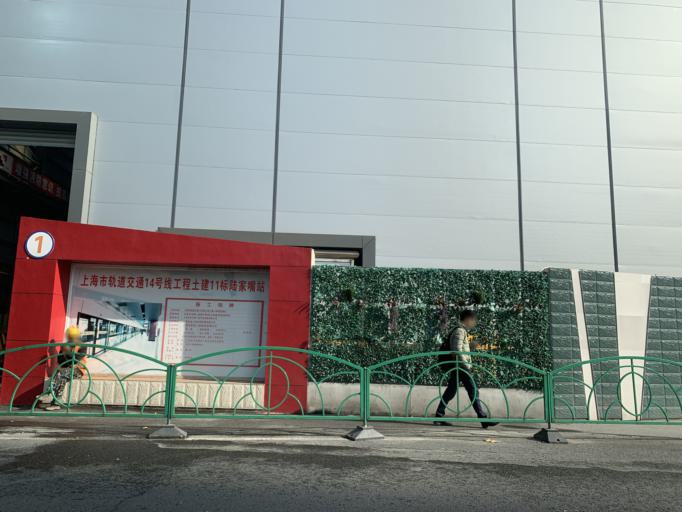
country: CN
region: Shanghai Shi
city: Hongkou
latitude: 31.2363
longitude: 121.4971
